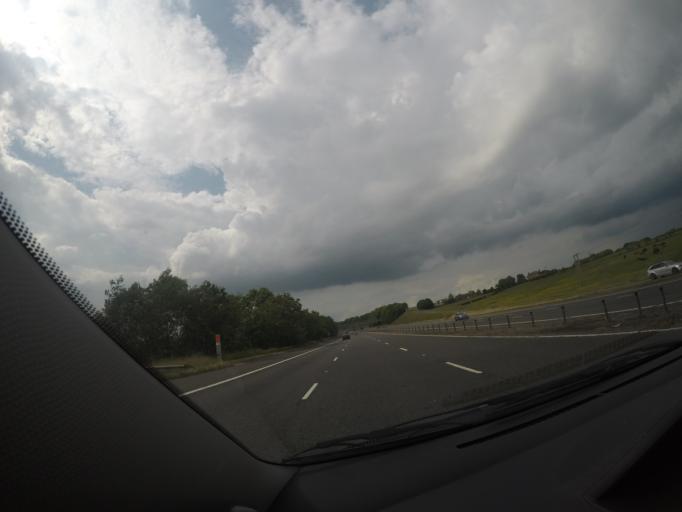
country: GB
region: Scotland
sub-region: Dumfries and Galloway
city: Annan
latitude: 55.0600
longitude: -3.2576
